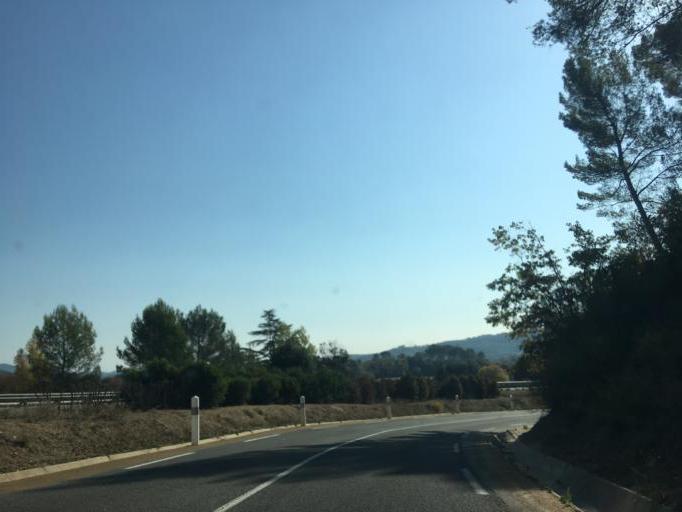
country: FR
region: Provence-Alpes-Cote d'Azur
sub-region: Departement du Var
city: Figanieres
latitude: 43.5716
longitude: 6.5065
